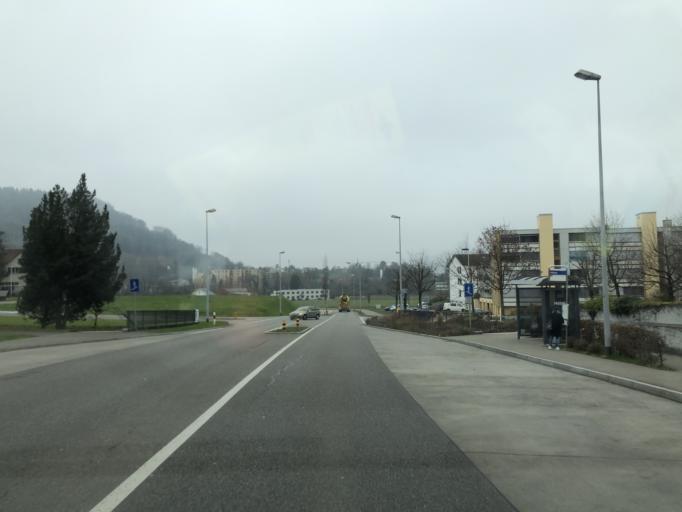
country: CH
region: Aargau
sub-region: Bezirk Baden
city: Turgi
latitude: 47.4938
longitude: 8.2638
